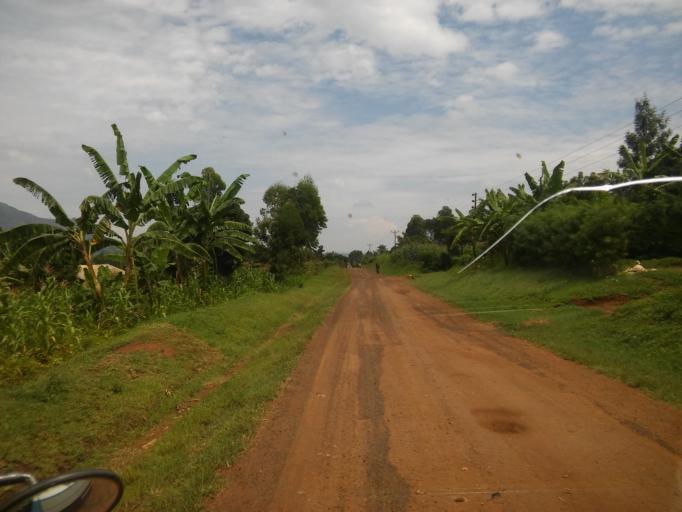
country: UG
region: Eastern Region
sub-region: Bududa District
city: Bududa
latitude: 0.9169
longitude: 34.2776
